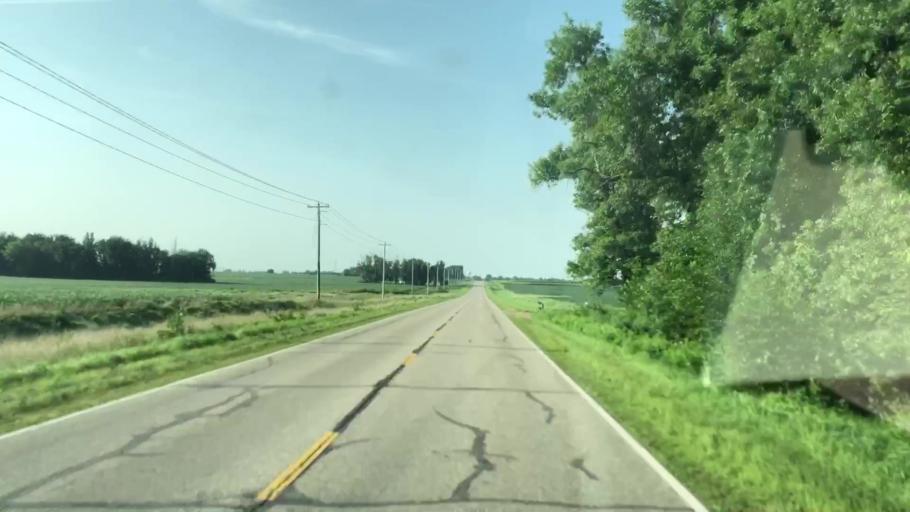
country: US
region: Iowa
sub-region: Lyon County
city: George
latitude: 43.3662
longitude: -95.9983
